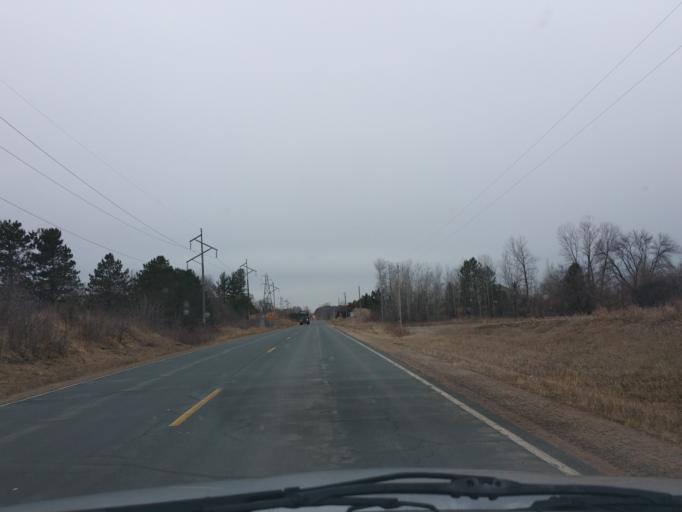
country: US
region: Wisconsin
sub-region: Saint Croix County
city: Roberts
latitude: 45.0357
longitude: -92.6247
